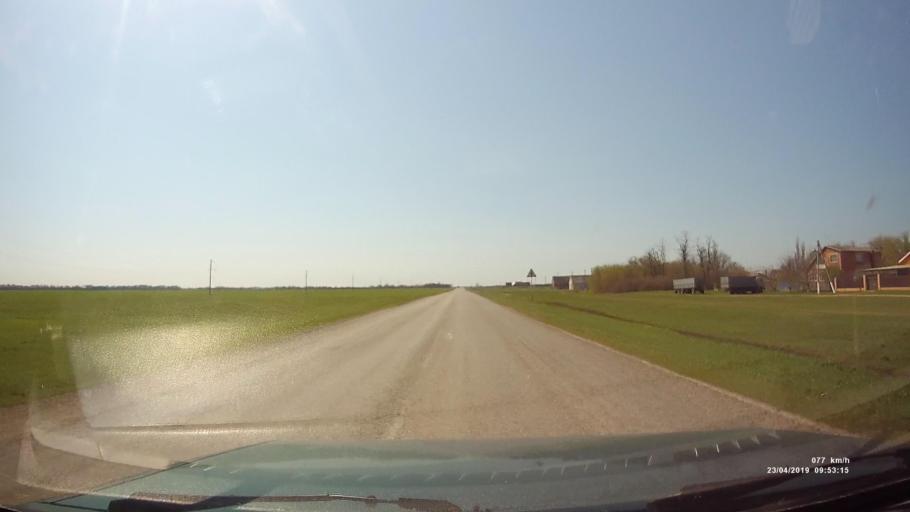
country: RU
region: Rostov
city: Orlovskiy
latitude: 46.8352
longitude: 42.0495
